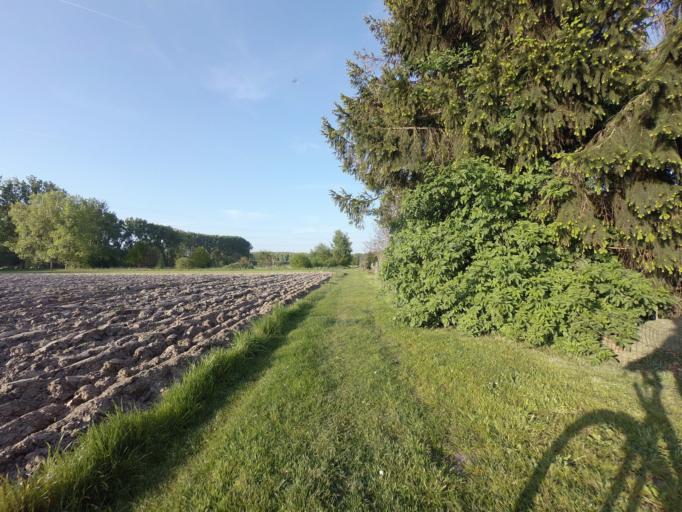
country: BE
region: Flanders
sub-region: Provincie Vlaams-Brabant
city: Zemst
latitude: 50.9514
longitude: 4.4638
